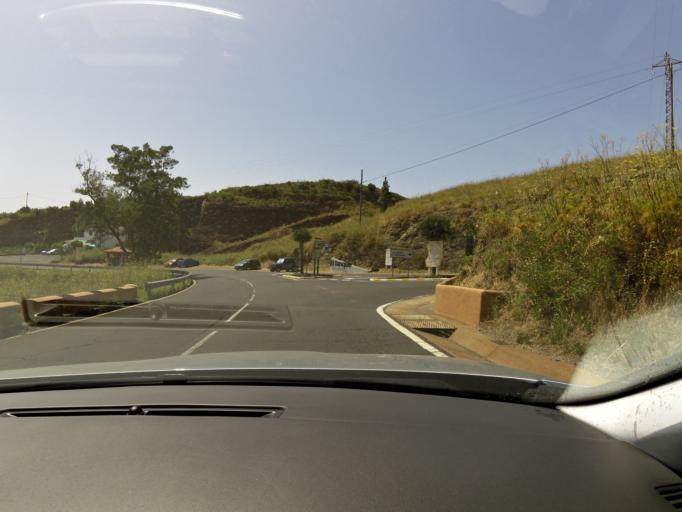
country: ES
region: Canary Islands
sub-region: Provincia de Santa Cruz de Tenerife
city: Santiago del Teide
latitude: 28.3175
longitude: -16.8042
